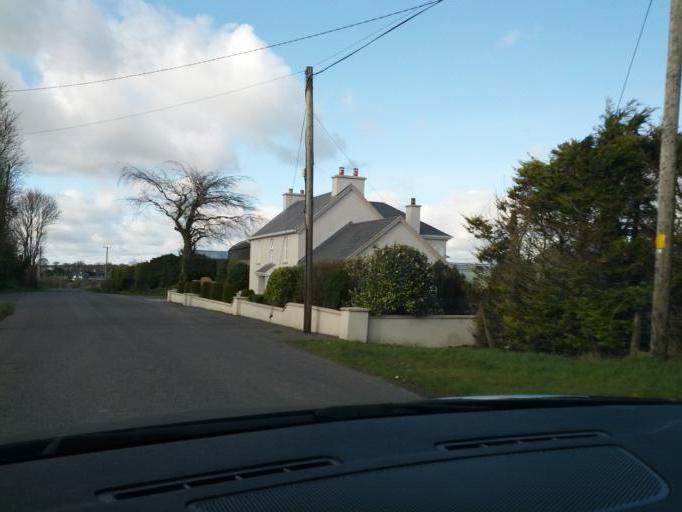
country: IE
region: Connaught
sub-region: County Galway
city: Athenry
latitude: 53.4745
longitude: -8.5692
